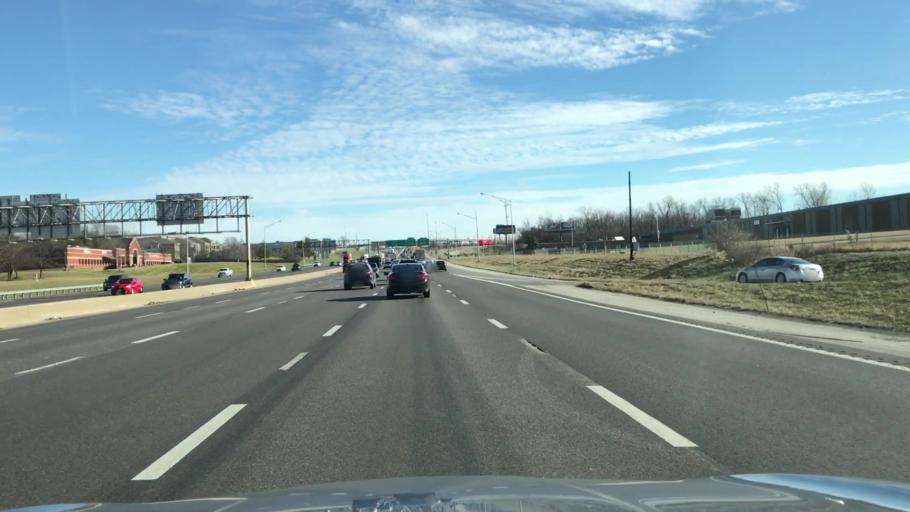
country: US
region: Missouri
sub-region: Saint Charles County
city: Saint Charles
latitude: 38.7539
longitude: -90.4551
